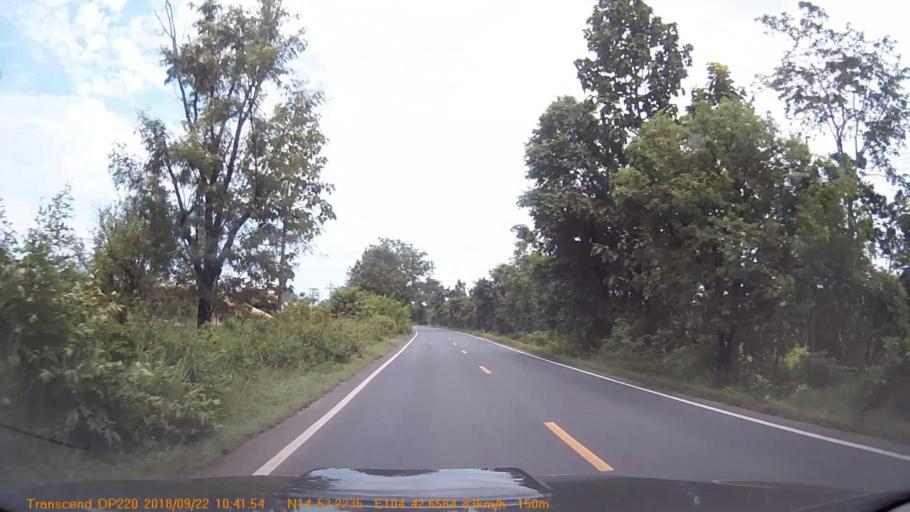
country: TH
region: Sisaket
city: Non Kho
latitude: 14.8869
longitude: 104.7109
